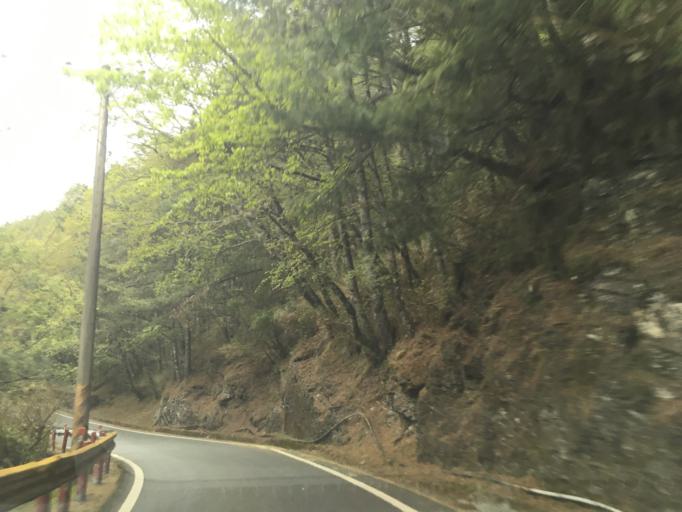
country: TW
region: Taiwan
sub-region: Hualien
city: Hualian
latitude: 24.1809
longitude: 121.3200
